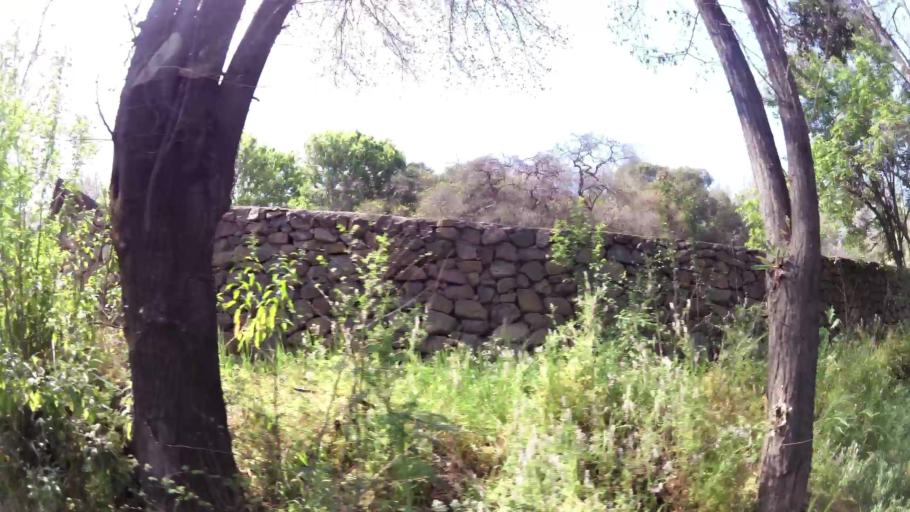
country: CL
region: Santiago Metropolitan
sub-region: Provincia de Santiago
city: Villa Presidente Frei, Nunoa, Santiago, Chile
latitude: -33.4680
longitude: -70.5235
